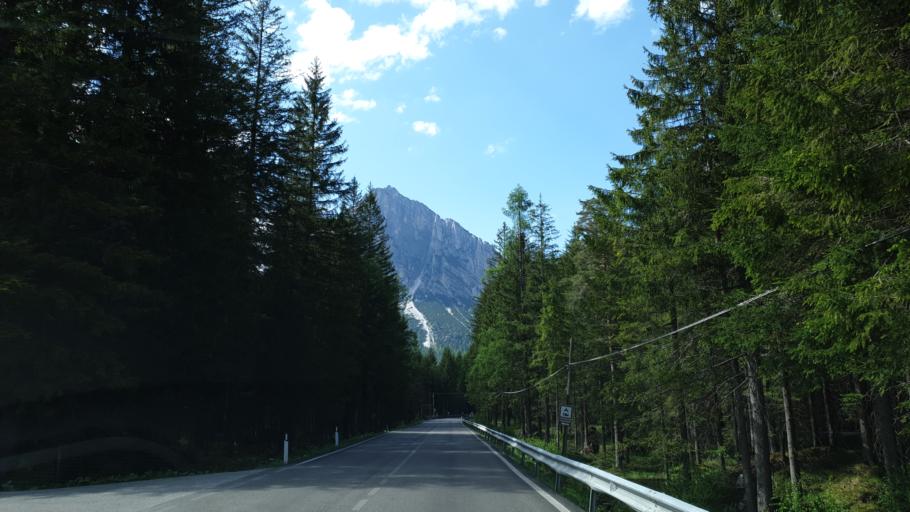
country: IT
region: Veneto
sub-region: Provincia di Belluno
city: Cortina d'Ampezzo
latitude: 46.5676
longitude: 12.1204
